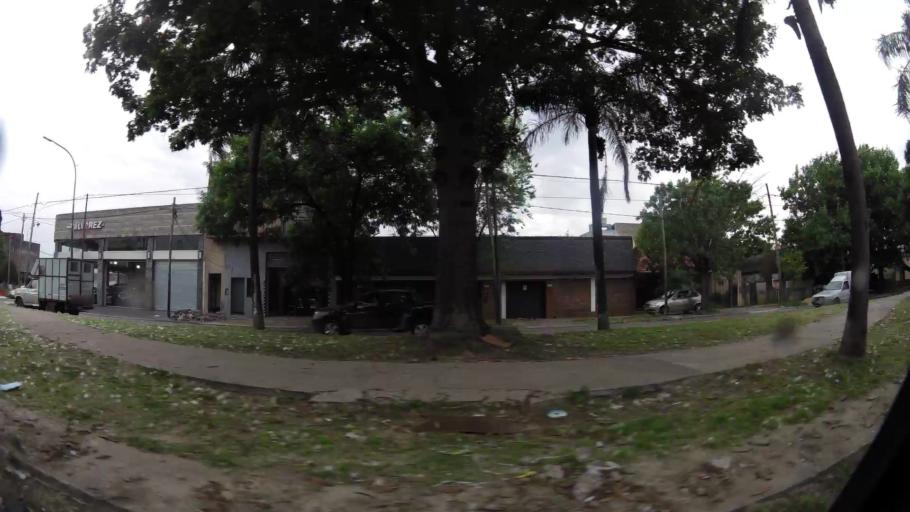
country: AR
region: Buenos Aires
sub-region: Partido de Lanus
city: Lanus
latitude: -34.6839
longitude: -58.4004
